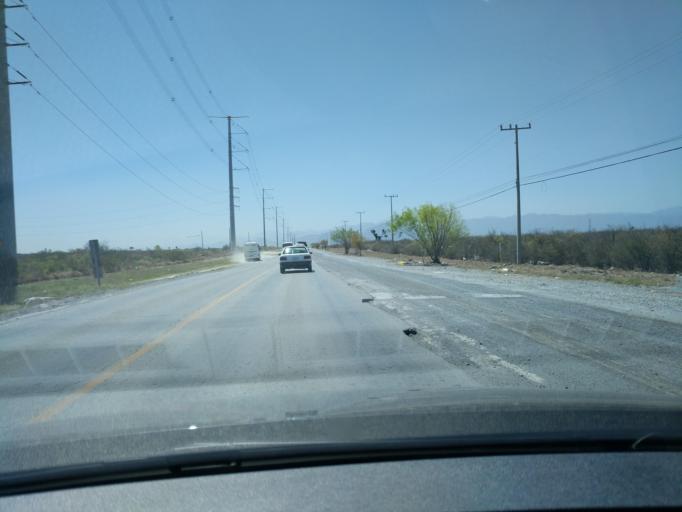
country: MX
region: Nuevo Leon
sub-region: Apodaca
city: Artemio Trevino
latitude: 25.8294
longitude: -100.1426
